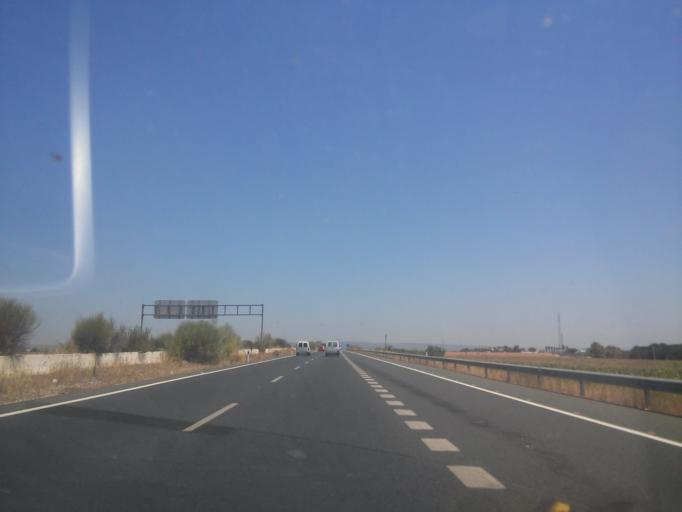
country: ES
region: Andalusia
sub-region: Provincia de Sevilla
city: La Rinconada
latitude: 37.4569
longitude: -5.9695
